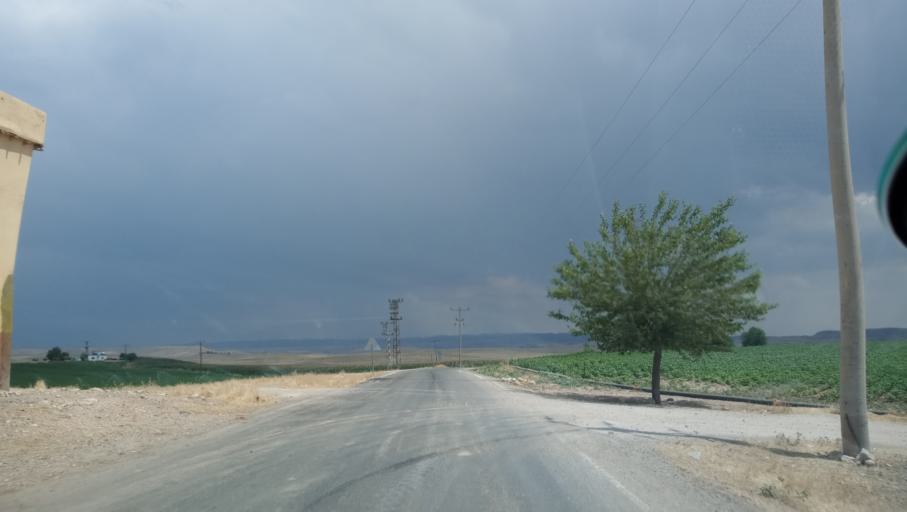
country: TR
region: Mardin
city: Baskavak
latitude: 37.6790
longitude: 40.8487
